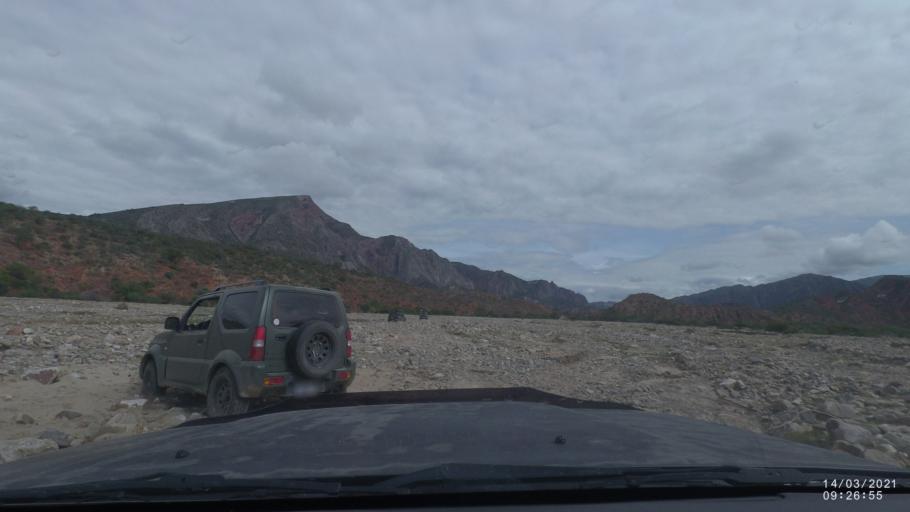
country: BO
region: Cochabamba
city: Cliza
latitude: -17.9478
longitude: -65.8560
